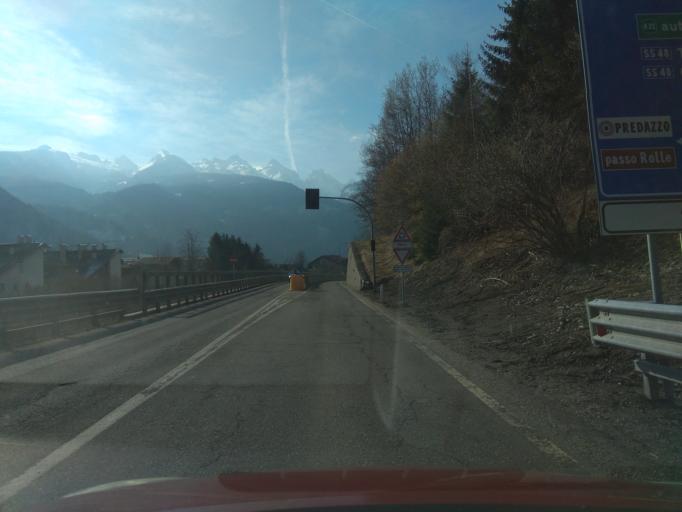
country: IT
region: Trentino-Alto Adige
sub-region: Provincia di Trento
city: Predazzo
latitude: 46.3122
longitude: 11.5958
